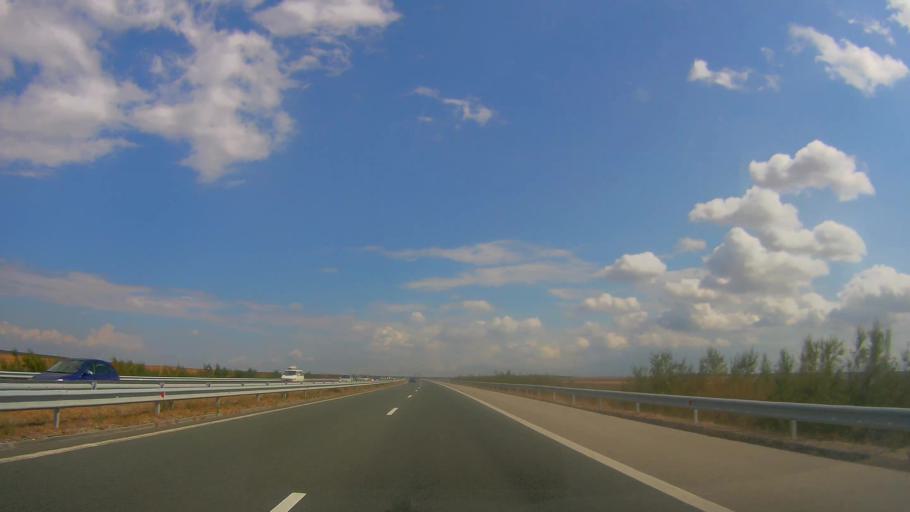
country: BG
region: Yambol
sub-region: Obshtina Straldzha
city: Straldzha
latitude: 42.5485
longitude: 26.7443
